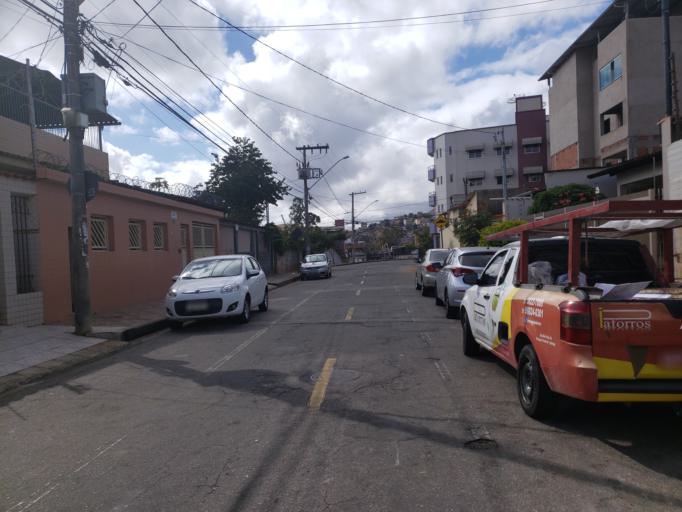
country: BR
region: Minas Gerais
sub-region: Ipatinga
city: Ipatinga
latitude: -19.4580
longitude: -42.5621
